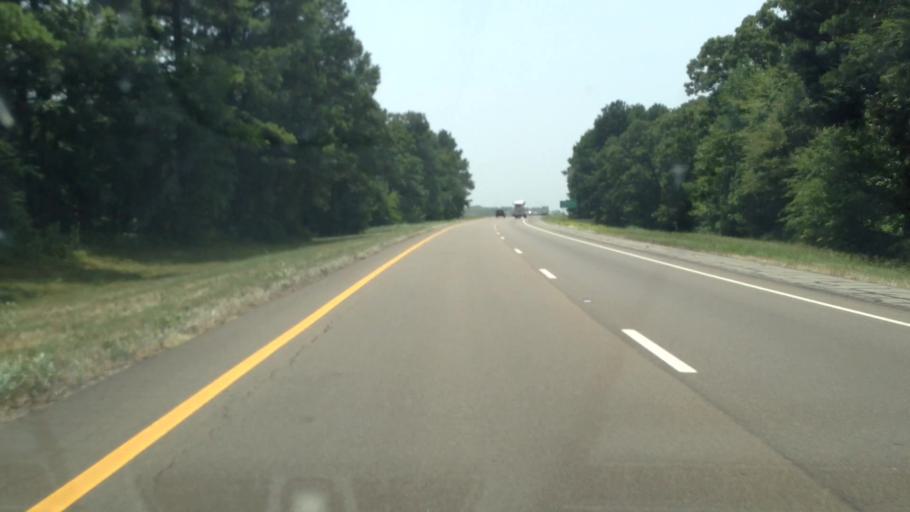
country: US
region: Texas
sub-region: Morris County
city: Naples
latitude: 33.2966
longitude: -94.7203
